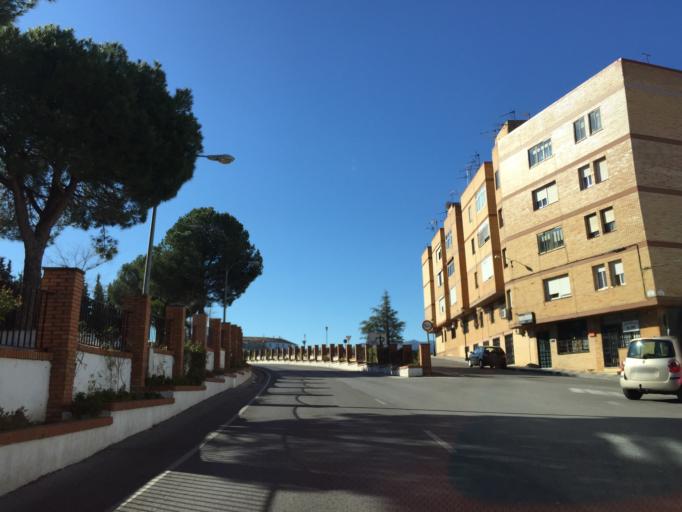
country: ES
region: Andalusia
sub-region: Provincia de Malaga
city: Ronda
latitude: 36.7511
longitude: -5.1701
